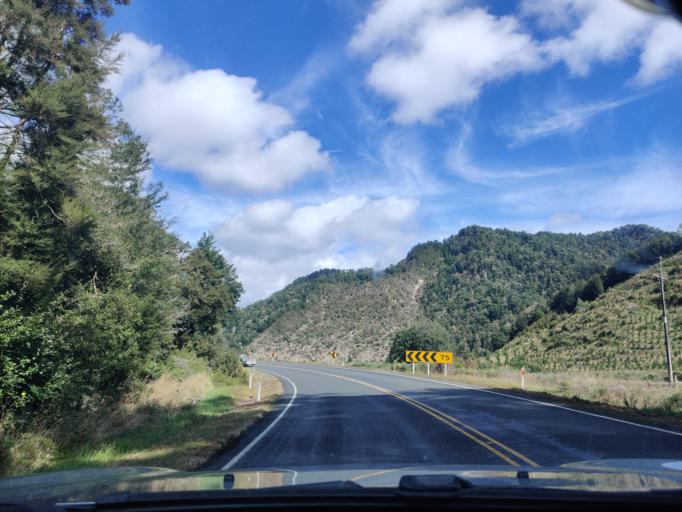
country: NZ
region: Tasman
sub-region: Tasman District
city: Wakefield
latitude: -41.7389
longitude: 172.3984
